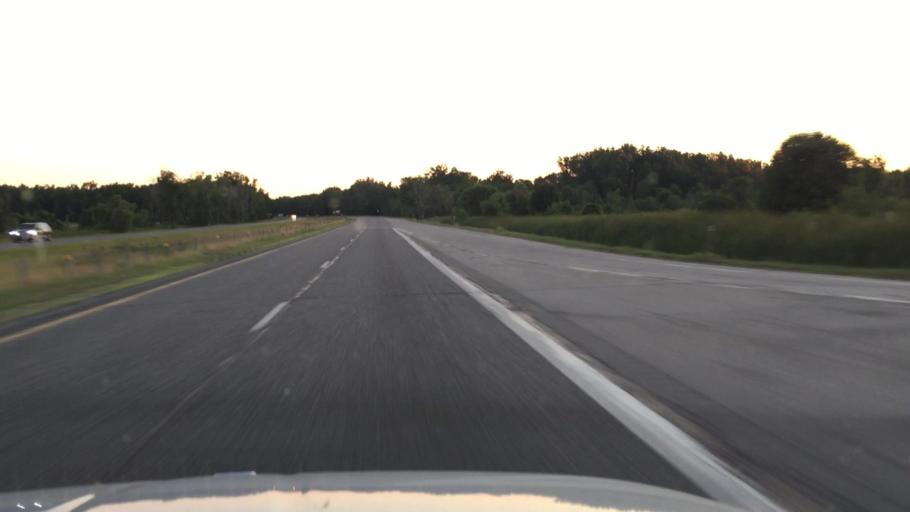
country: US
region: Michigan
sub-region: Shiawassee County
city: Corunna
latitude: 42.8932
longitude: -84.0978
